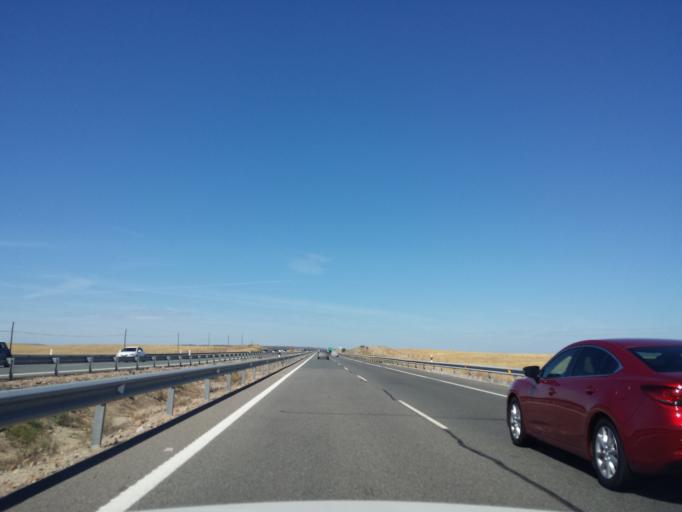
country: ES
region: Extremadura
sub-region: Provincia de Caceres
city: Peraleda de la Mata
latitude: 39.8922
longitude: -5.3890
